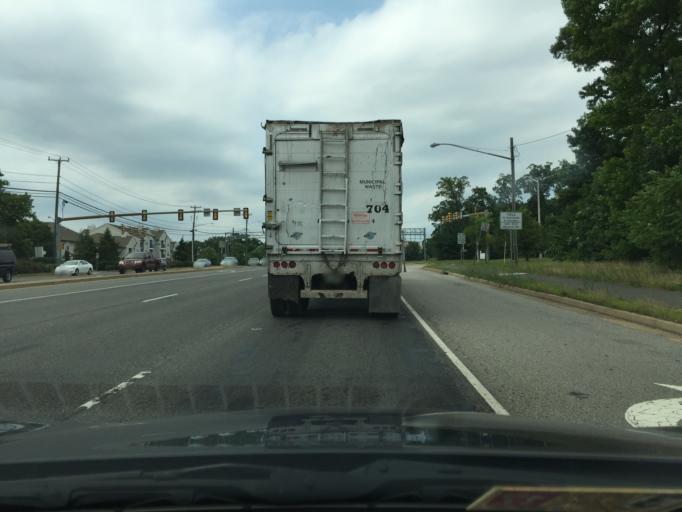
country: US
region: Virginia
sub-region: Fairfax County
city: Franconia
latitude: 38.7910
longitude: -77.1368
